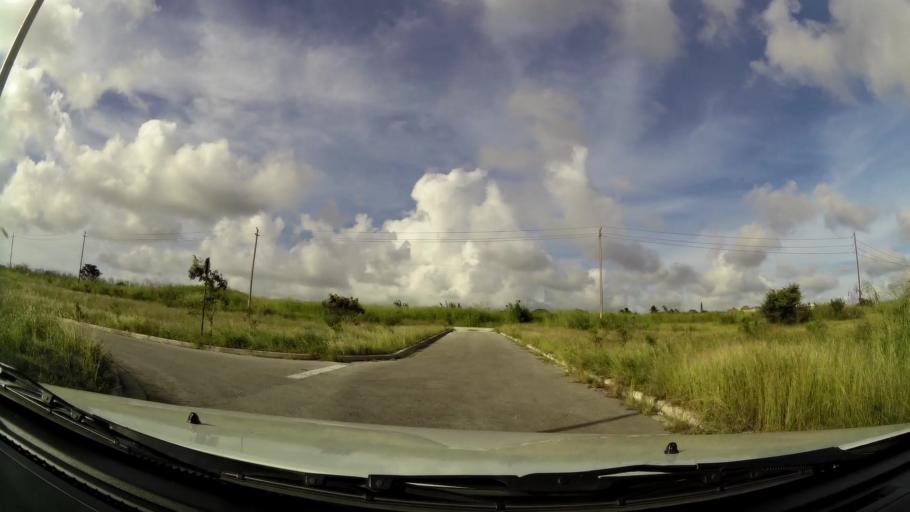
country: BB
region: Christ Church
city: Oistins
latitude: 13.0862
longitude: -59.5605
